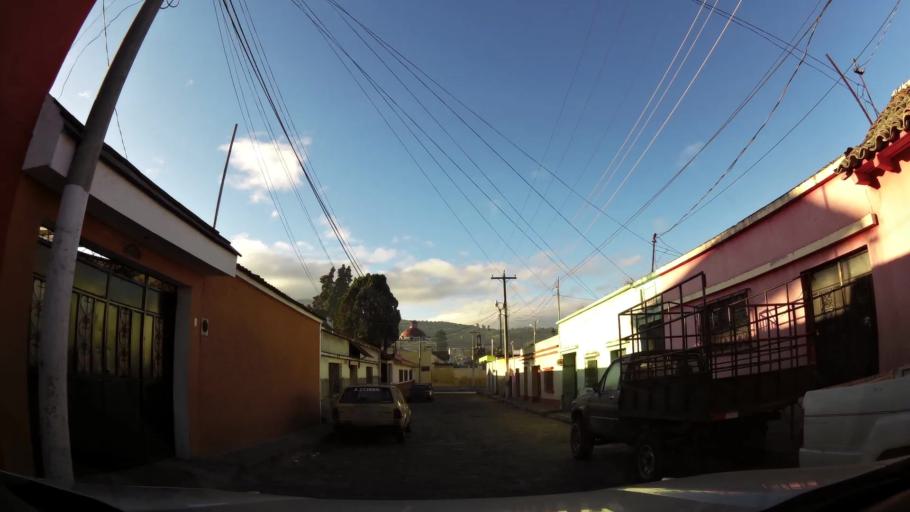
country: GT
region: Quetzaltenango
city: Quetzaltenango
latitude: 14.8378
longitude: -91.5259
